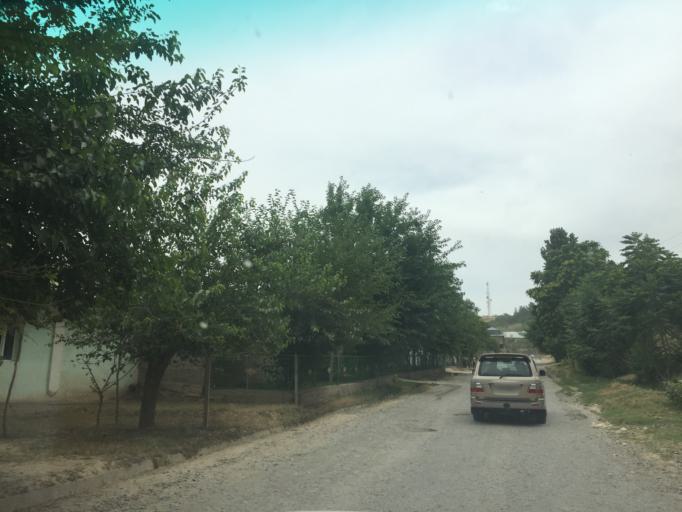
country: TJ
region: Khatlon
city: Kulob
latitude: 37.9010
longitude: 69.7990
